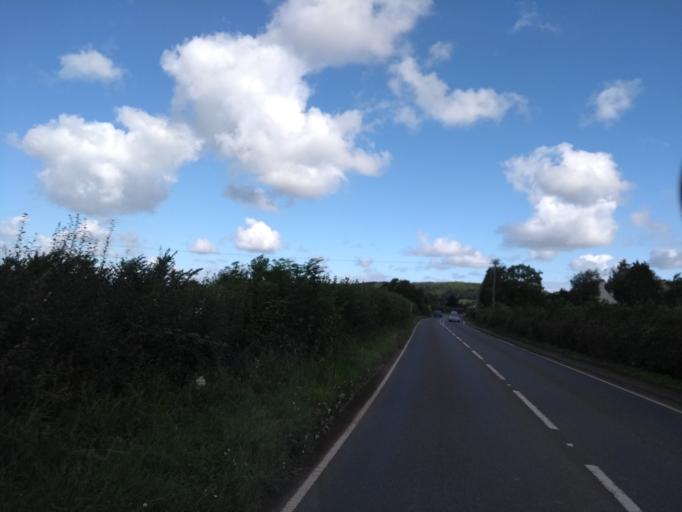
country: GB
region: England
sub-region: Somerset
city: Street
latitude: 51.0942
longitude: -2.7315
